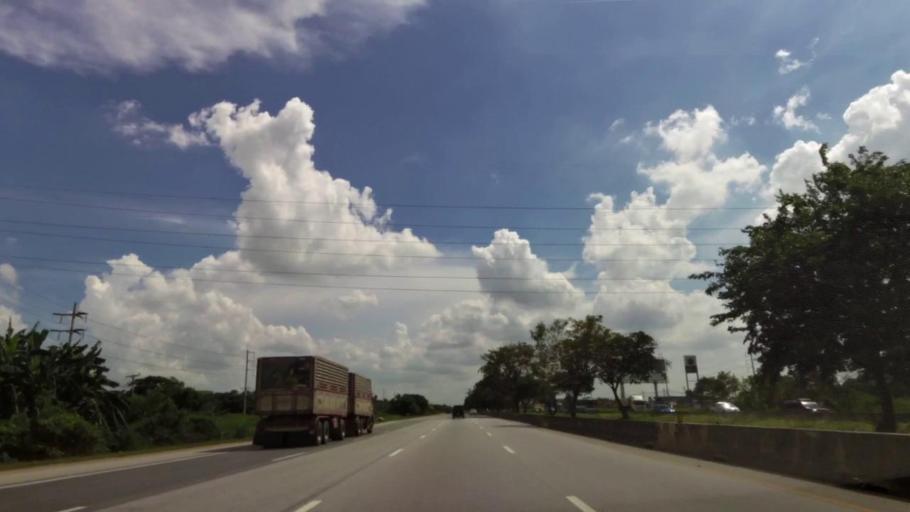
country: TH
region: Phra Nakhon Si Ayutthaya
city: Maha Rat
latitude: 14.5044
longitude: 100.5204
